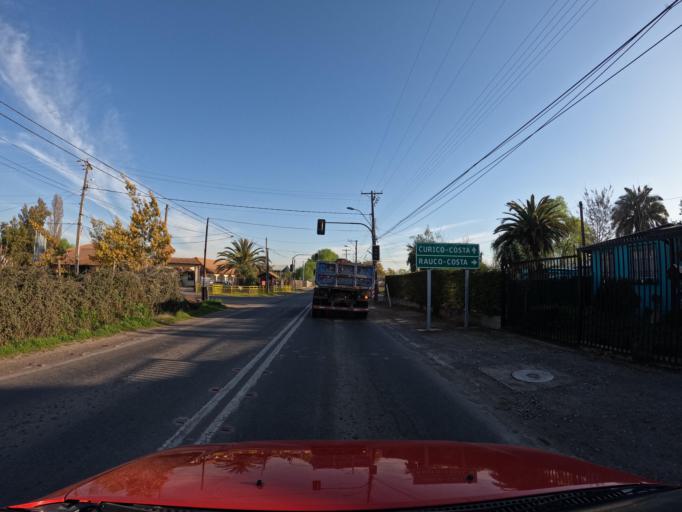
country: CL
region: Maule
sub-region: Provincia de Curico
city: Rauco
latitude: -34.8883
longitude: -71.2732
